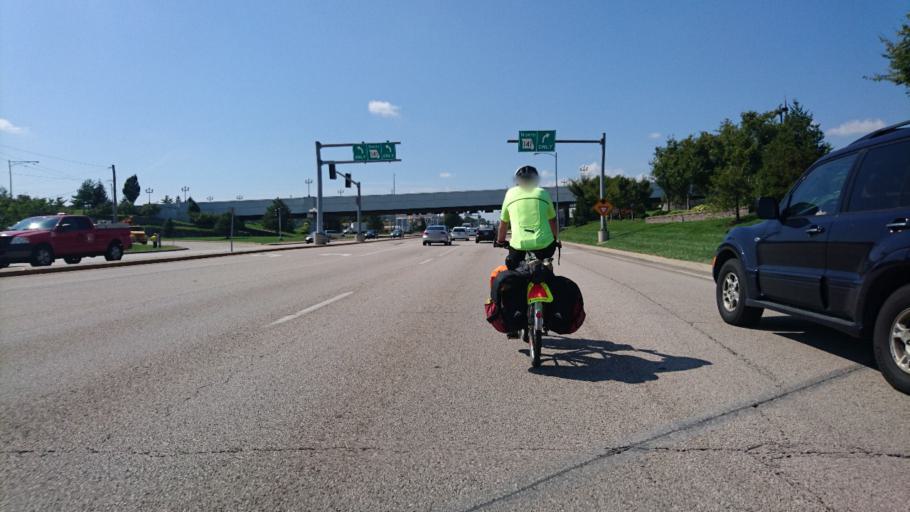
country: US
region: Missouri
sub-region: Saint Louis County
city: Manchester
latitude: 38.5929
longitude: -90.5071
